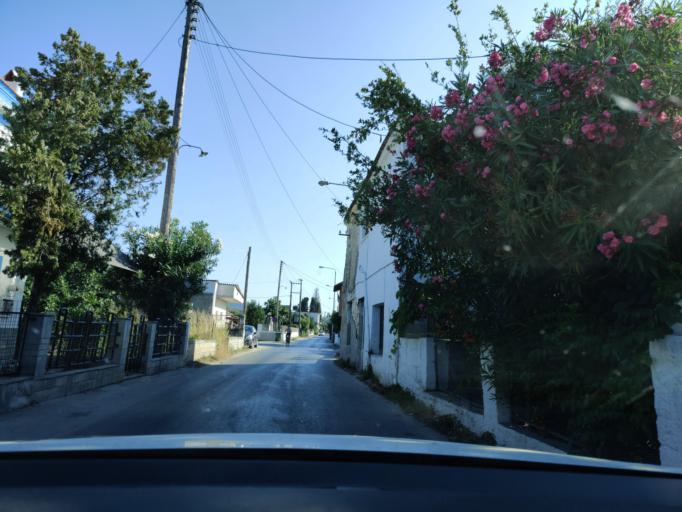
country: GR
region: East Macedonia and Thrace
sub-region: Nomos Kavalas
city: Prinos
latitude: 40.7075
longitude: 24.5340
